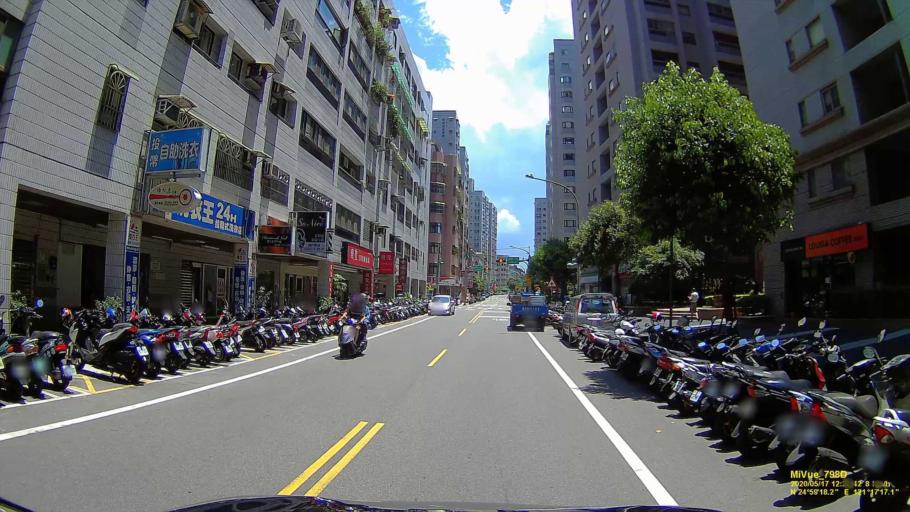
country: TW
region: Taiwan
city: Taoyuan City
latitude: 24.9883
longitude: 121.2880
